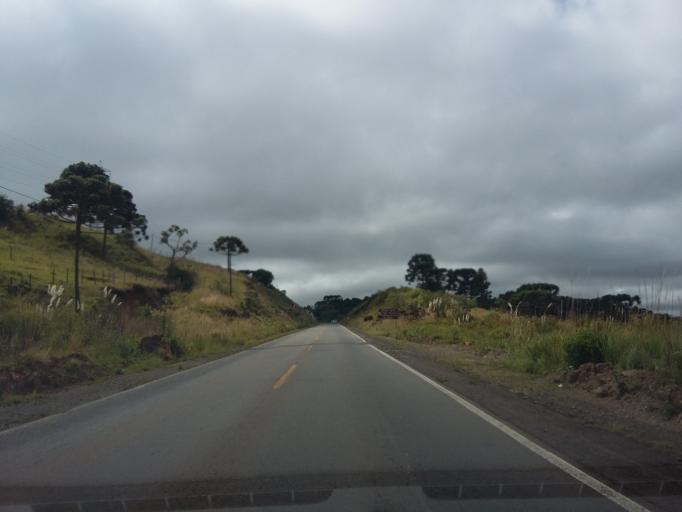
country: BR
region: Santa Catarina
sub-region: Lages
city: Lages
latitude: -27.8873
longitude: -50.1616
